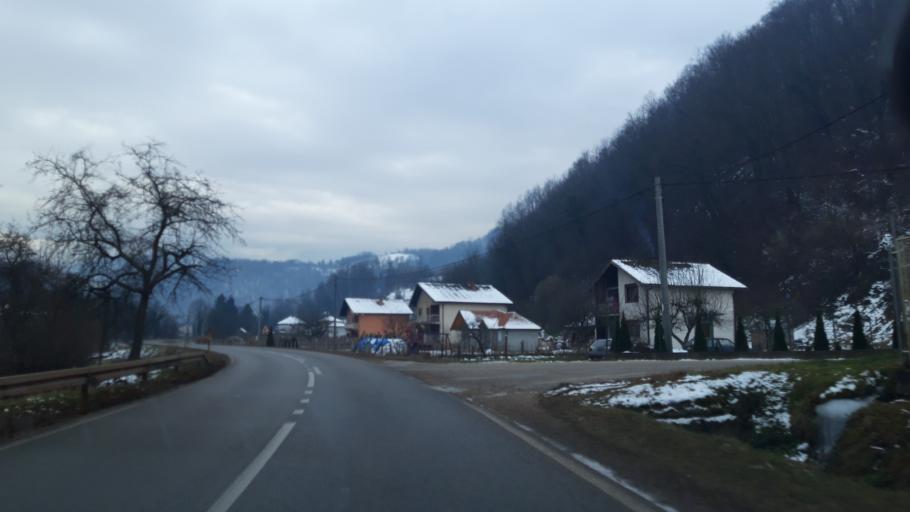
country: BA
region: Republika Srpska
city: Milici
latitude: 44.1837
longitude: 19.0755
